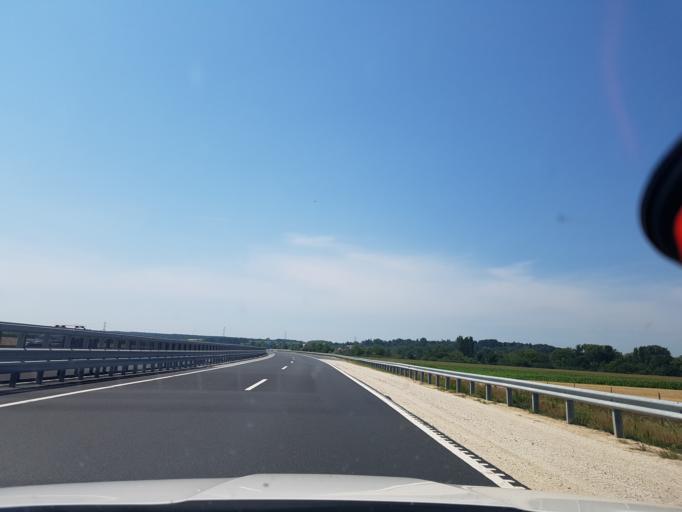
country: HU
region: Vas
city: Sarvar
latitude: 47.3157
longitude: 16.8416
